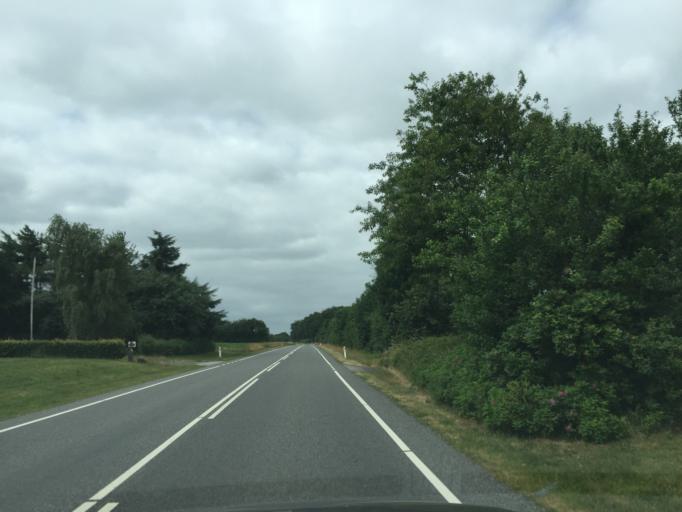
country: DK
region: South Denmark
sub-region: Vejen Kommune
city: Brorup
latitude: 55.4172
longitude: 8.9505
